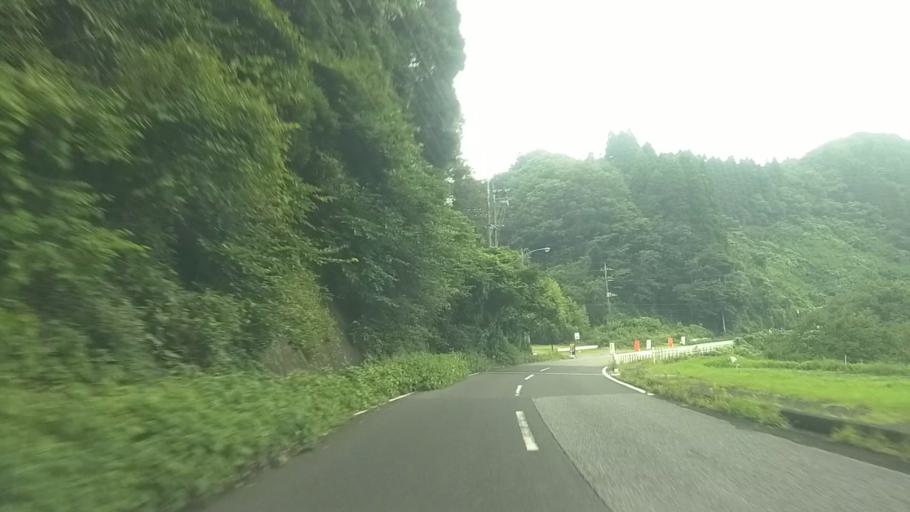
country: JP
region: Chiba
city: Katsuura
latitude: 35.2553
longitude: 140.2438
